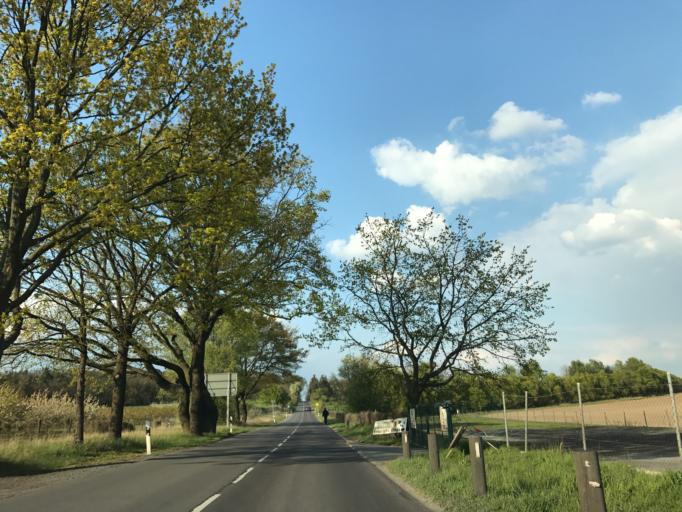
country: DE
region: Brandenburg
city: Wustermark
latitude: 52.4631
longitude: 12.9751
